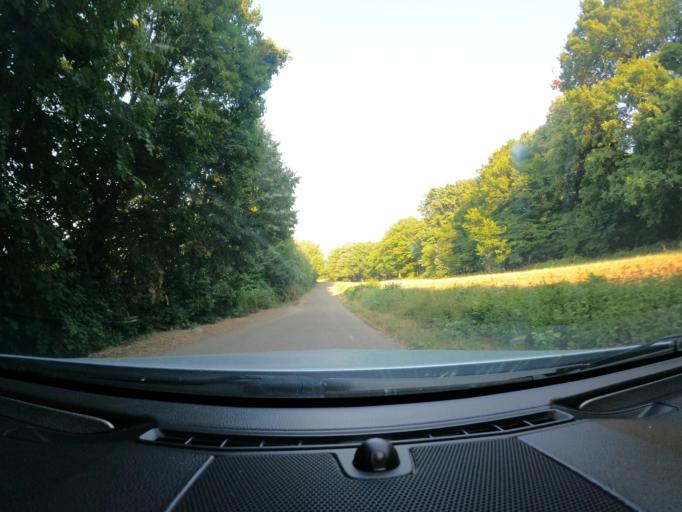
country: RS
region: Autonomna Pokrajina Vojvodina
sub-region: Juznobacki Okrug
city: Beocin
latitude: 45.1564
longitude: 19.7442
